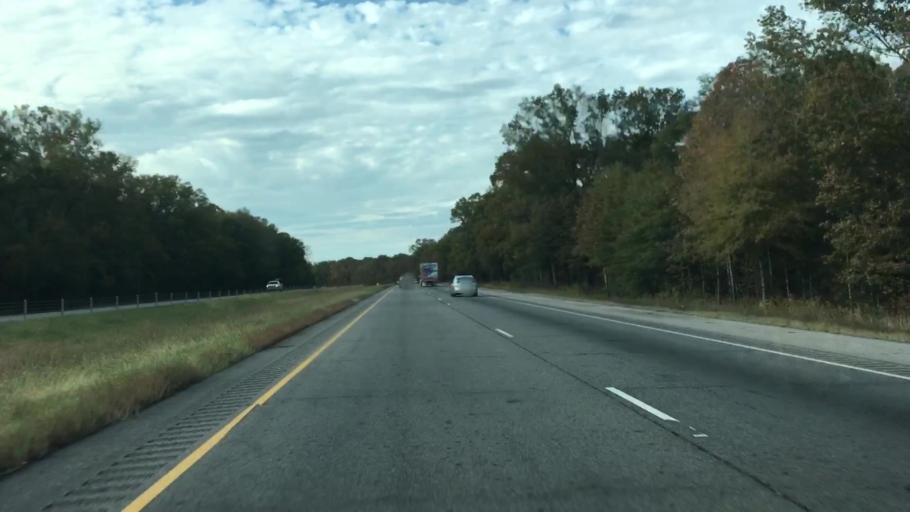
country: US
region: Arkansas
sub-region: Pope County
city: Atkins
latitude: 35.2422
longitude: -92.8605
